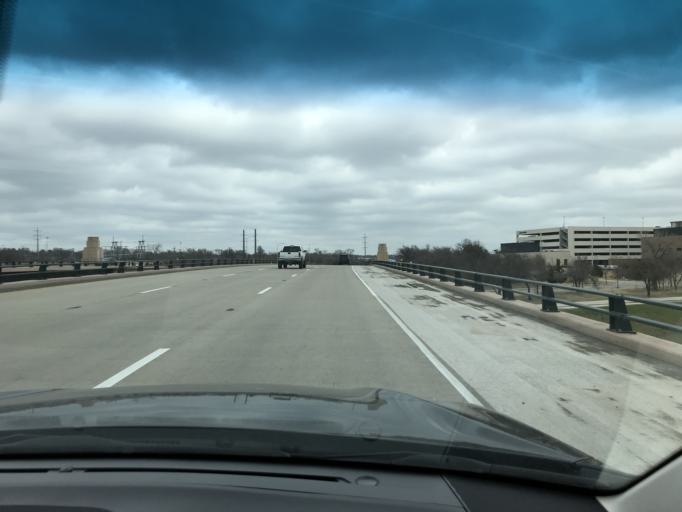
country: US
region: Texas
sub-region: Tarrant County
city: Westworth
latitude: 32.7061
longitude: -97.4048
